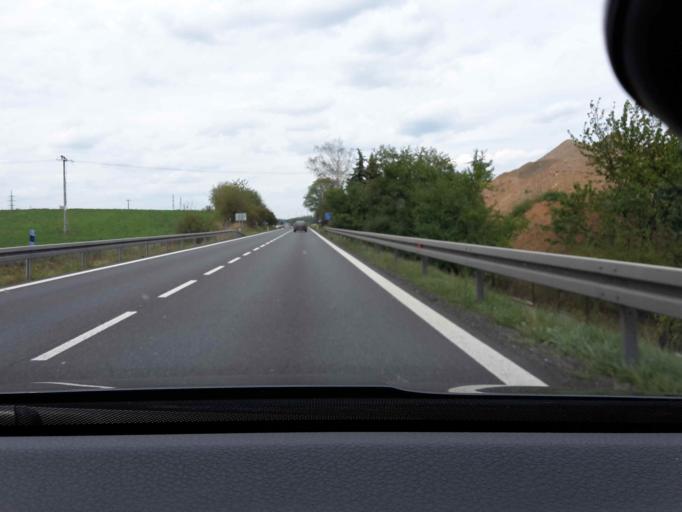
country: CZ
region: Central Bohemia
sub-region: Okres Benesov
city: Benesov
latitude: 49.7907
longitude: 14.6785
